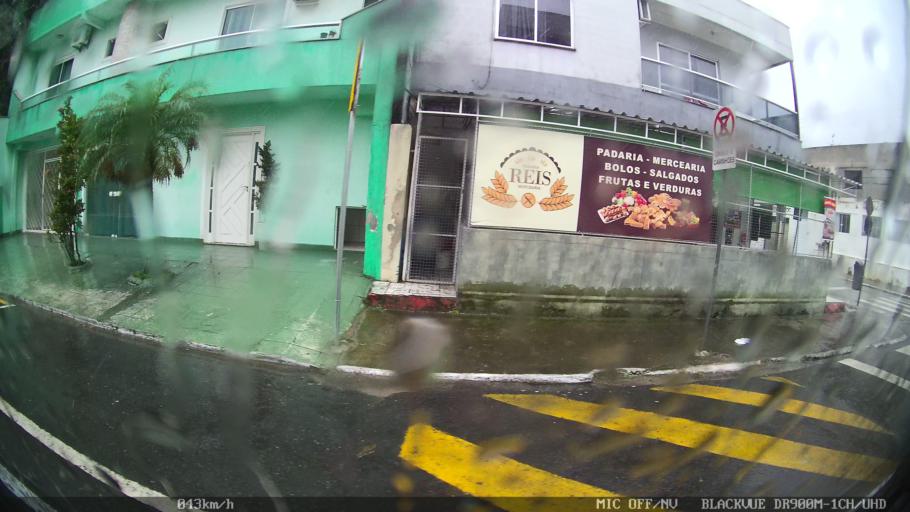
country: BR
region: Santa Catarina
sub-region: Balneario Camboriu
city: Balneario Camboriu
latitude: -27.0140
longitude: -48.6321
